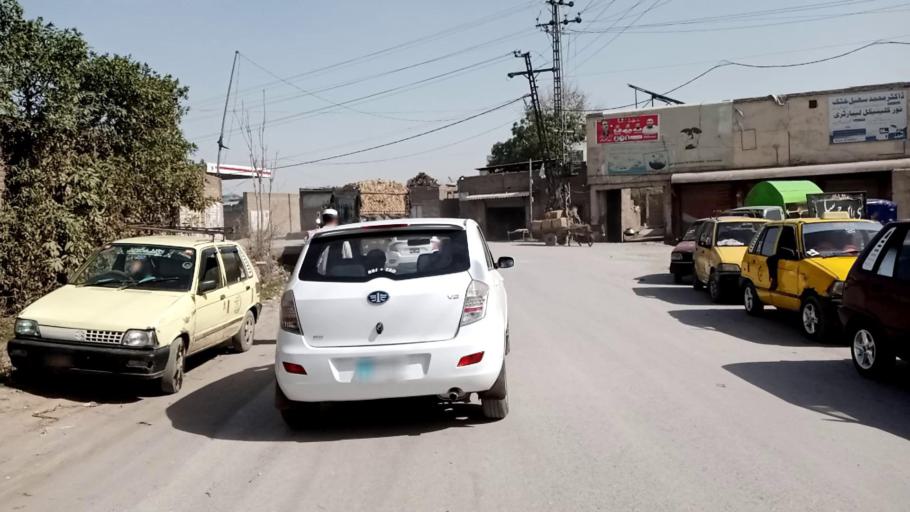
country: PK
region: Khyber Pakhtunkhwa
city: Peshawar
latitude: 34.0108
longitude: 71.6473
